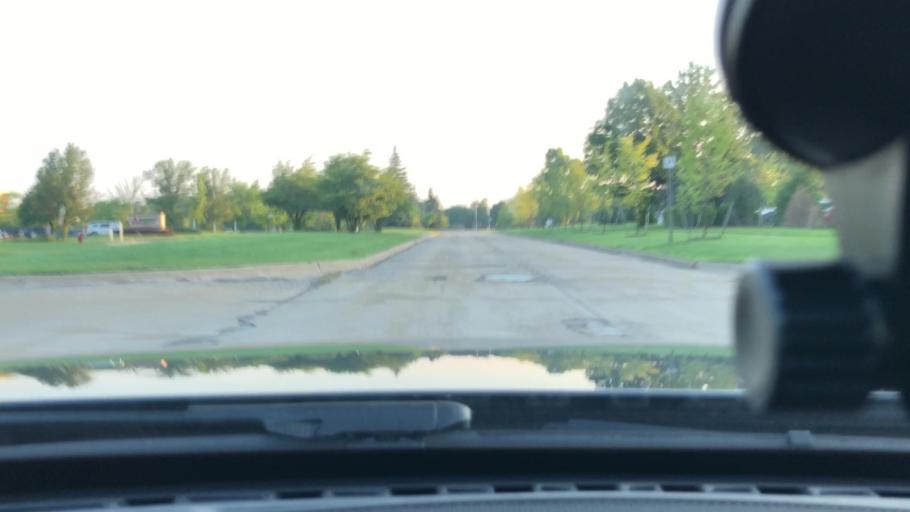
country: US
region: Michigan
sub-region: Wayne County
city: Plymouth
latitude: 42.3960
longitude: -83.5000
